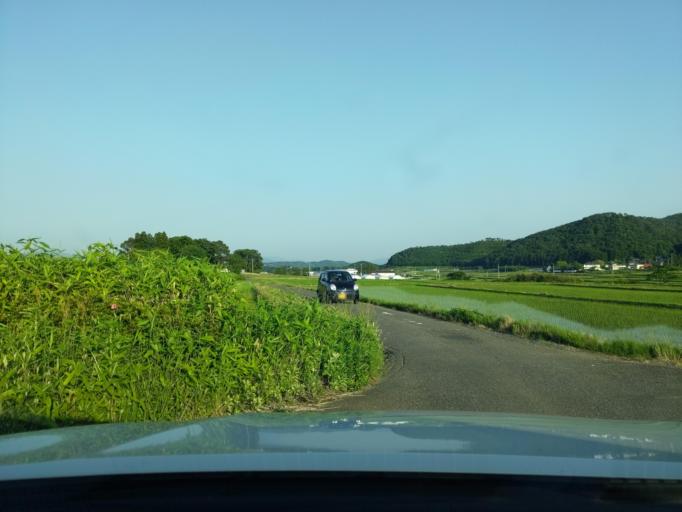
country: JP
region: Fukushima
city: Motomiya
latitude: 37.5251
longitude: 140.3654
